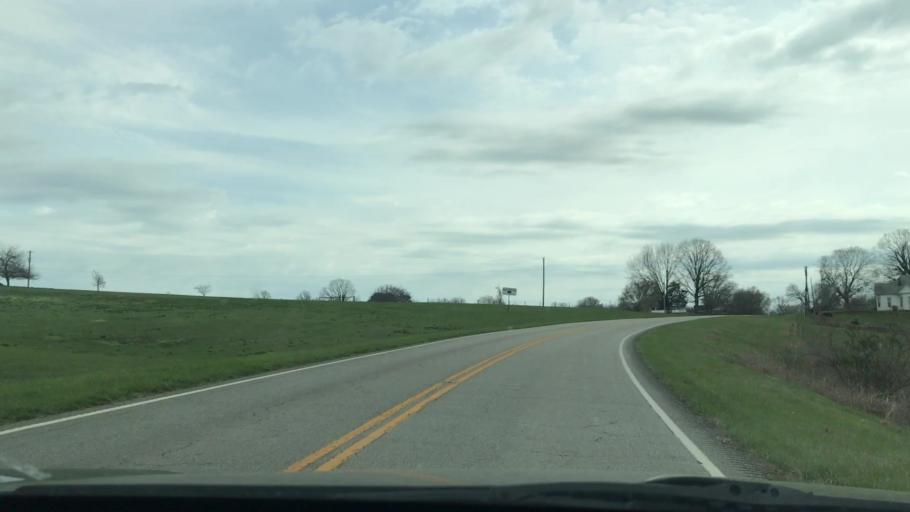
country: US
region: Kentucky
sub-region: Hart County
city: Munfordville
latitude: 37.2981
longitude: -85.7629
